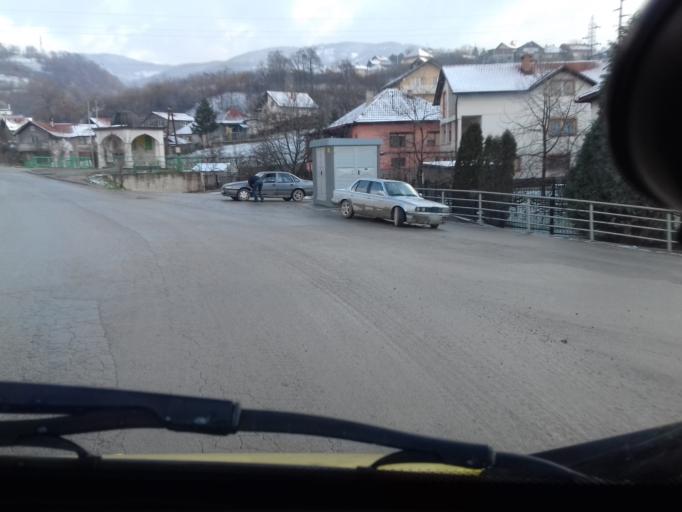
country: BA
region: Federation of Bosnia and Herzegovina
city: Zenica
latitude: 44.2206
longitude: 17.9160
